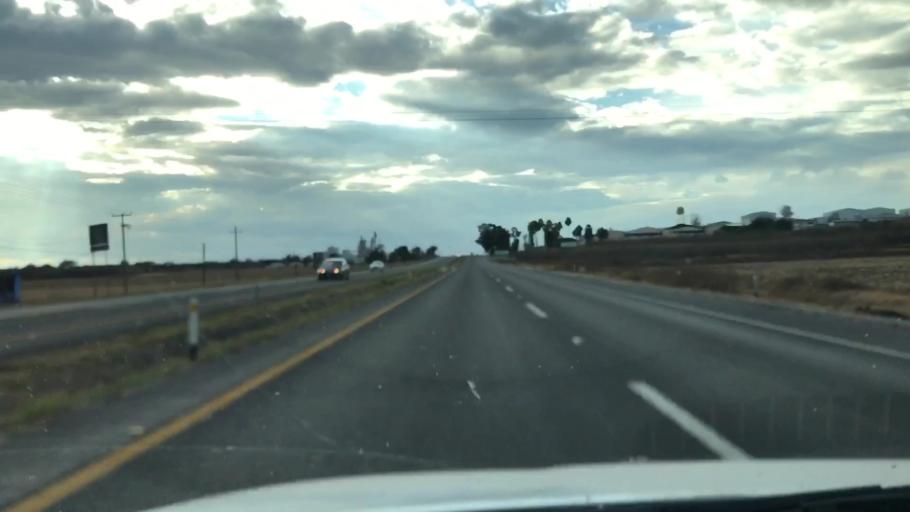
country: MX
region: Guanajuato
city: Penjamo
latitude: 20.3816
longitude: -101.8154
